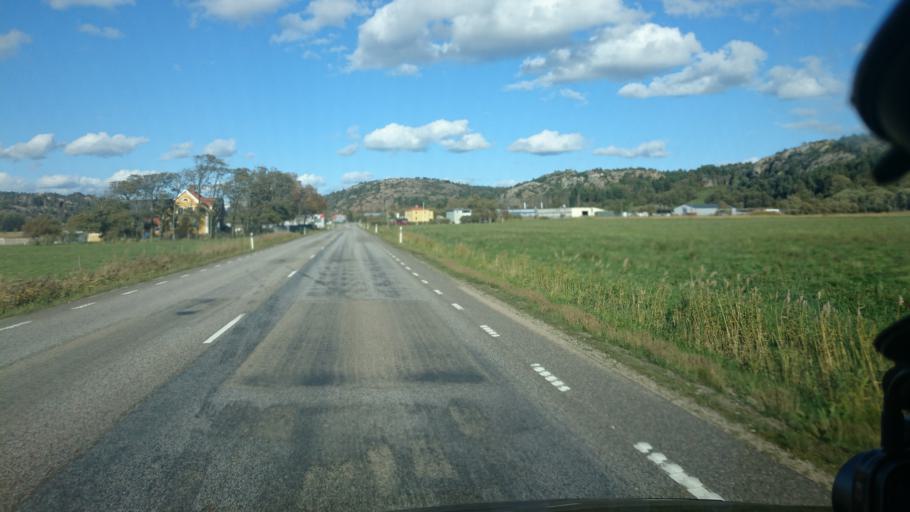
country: SE
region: Vaestra Goetaland
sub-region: Lysekils Kommun
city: Brastad
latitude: 58.3189
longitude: 11.4877
